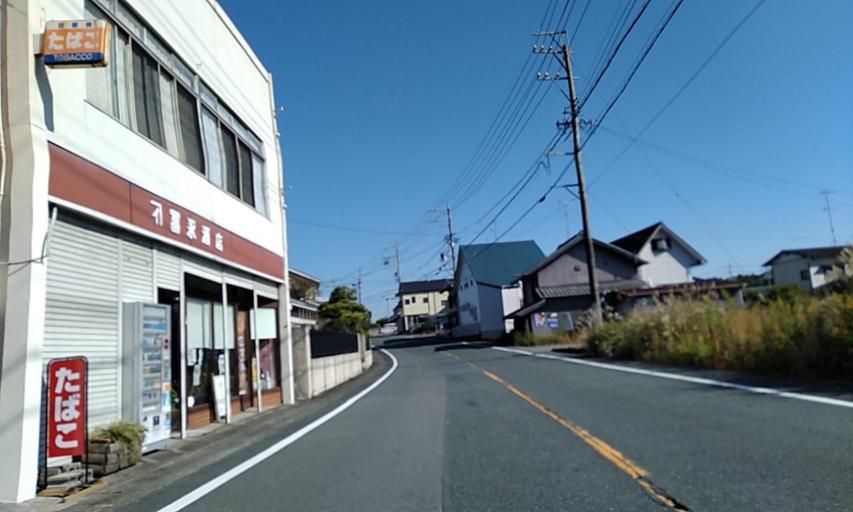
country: JP
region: Shizuoka
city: Hamakita
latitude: 34.8092
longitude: 137.6481
